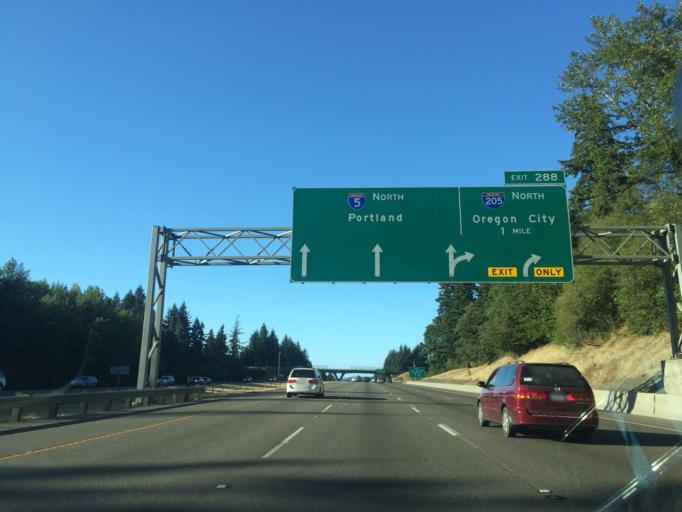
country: US
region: Oregon
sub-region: Washington County
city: Tualatin
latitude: 45.3503
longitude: -122.7653
